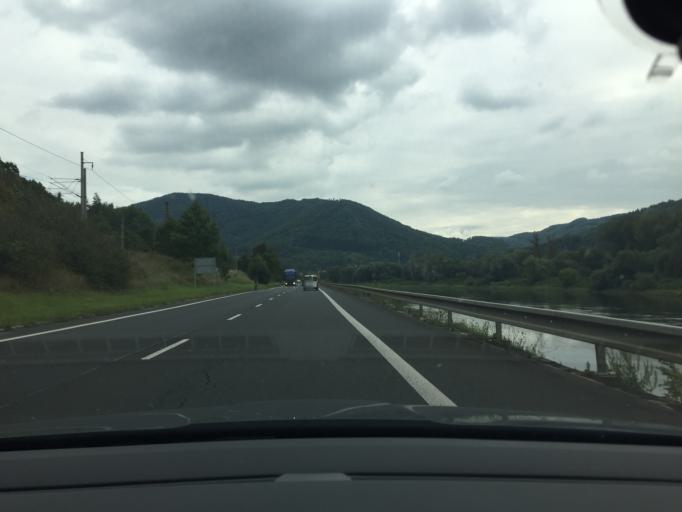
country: CZ
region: Ustecky
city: Velke Brezno
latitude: 50.6743
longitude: 14.1338
